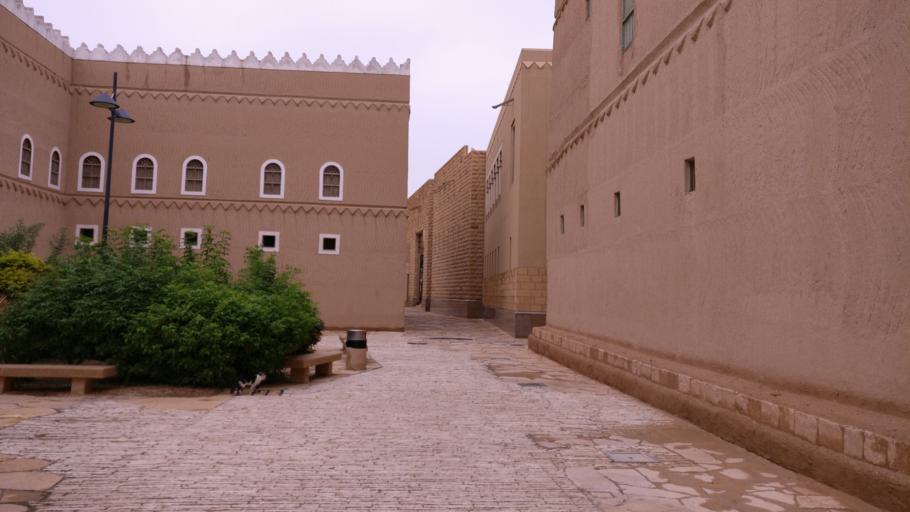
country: SA
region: Ar Riyad
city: Riyadh
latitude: 24.6465
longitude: 46.7090
